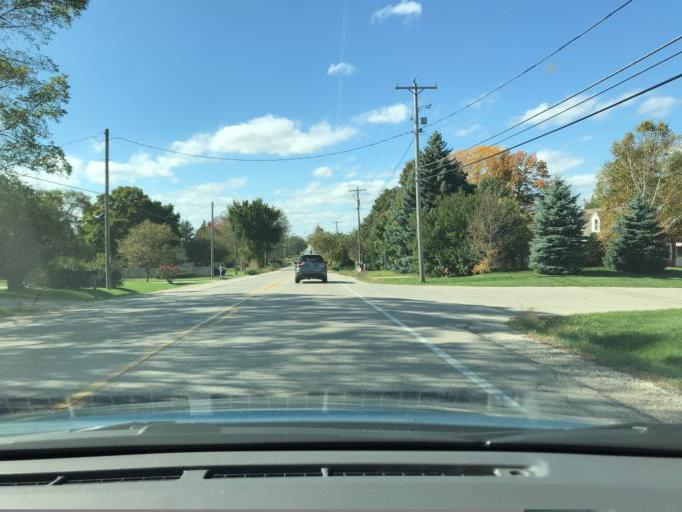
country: US
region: Wisconsin
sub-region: Kenosha County
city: Somers
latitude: 42.6034
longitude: -87.8870
